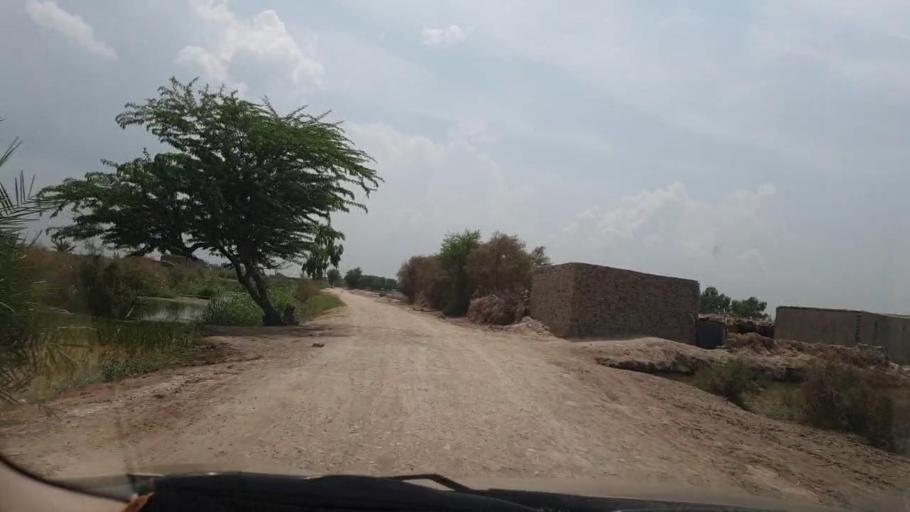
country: PK
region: Sindh
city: Larkana
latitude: 27.6203
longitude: 68.1554
